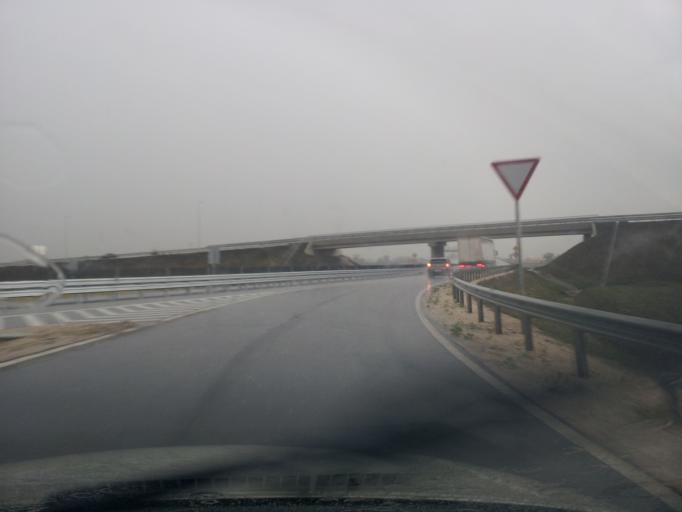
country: HU
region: Borsod-Abauj-Zemplen
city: Arnot
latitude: 48.1143
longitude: 20.8416
